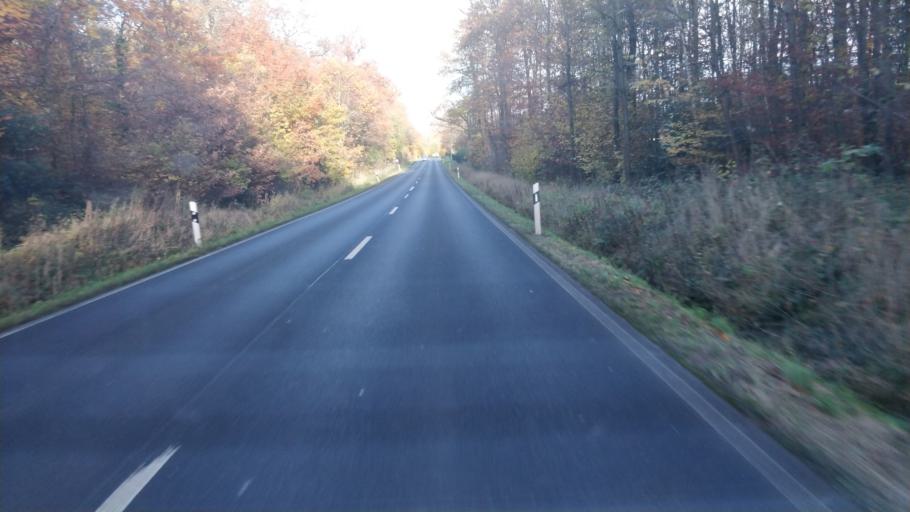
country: DE
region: North Rhine-Westphalia
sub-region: Regierungsbezirk Koln
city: Rheinbach
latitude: 50.6176
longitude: 6.9242
